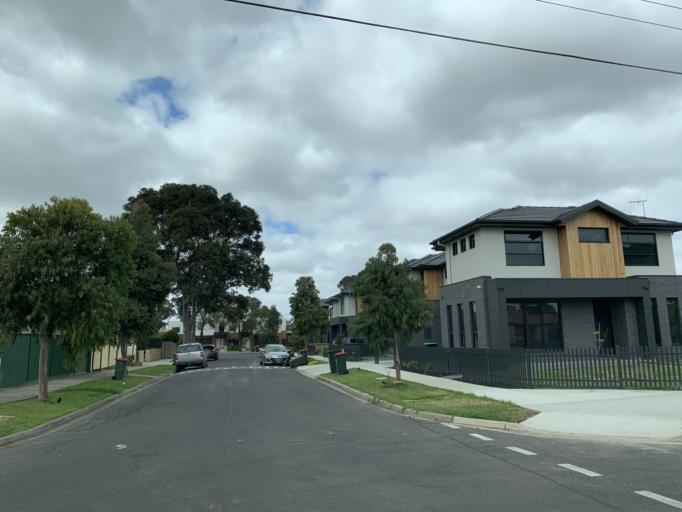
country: AU
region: Victoria
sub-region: Moonee Valley
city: Essendon West
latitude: -37.7635
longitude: 144.8602
